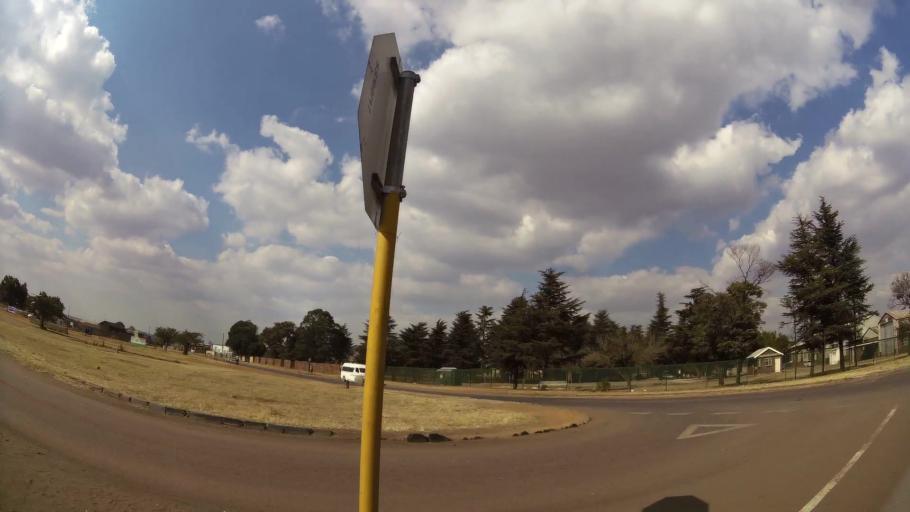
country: ZA
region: Mpumalanga
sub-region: Nkangala District Municipality
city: Delmas
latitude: -26.1338
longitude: 28.6839
